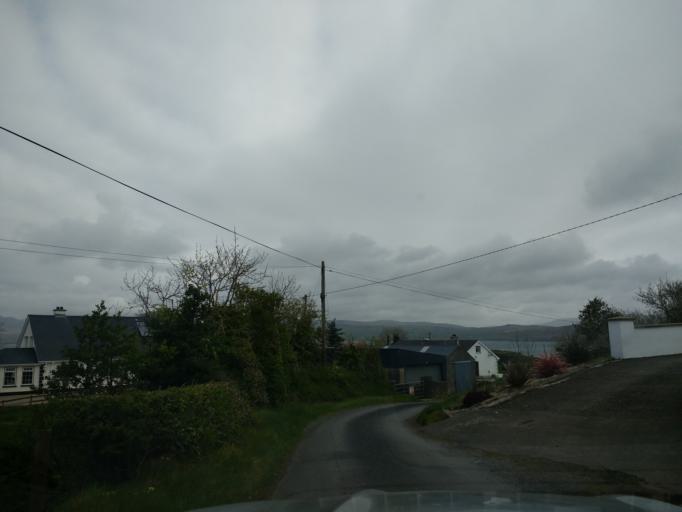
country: IE
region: Ulster
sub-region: County Donegal
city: Buncrana
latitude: 55.1342
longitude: -7.5284
